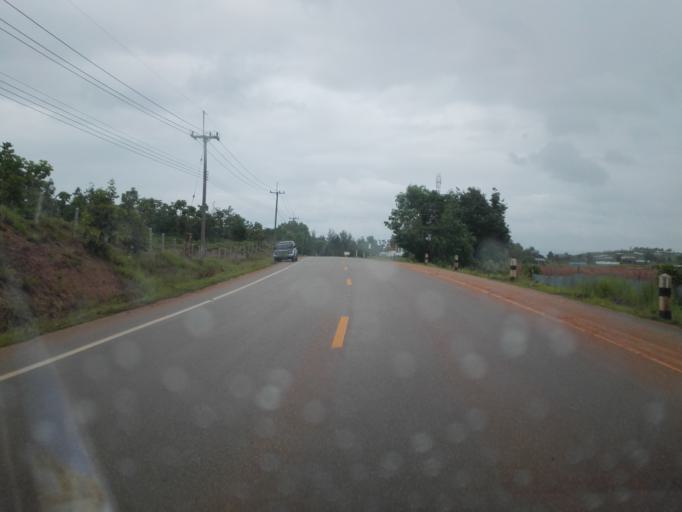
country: TH
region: Tak
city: Mae Sot
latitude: 16.6902
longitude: 98.4460
